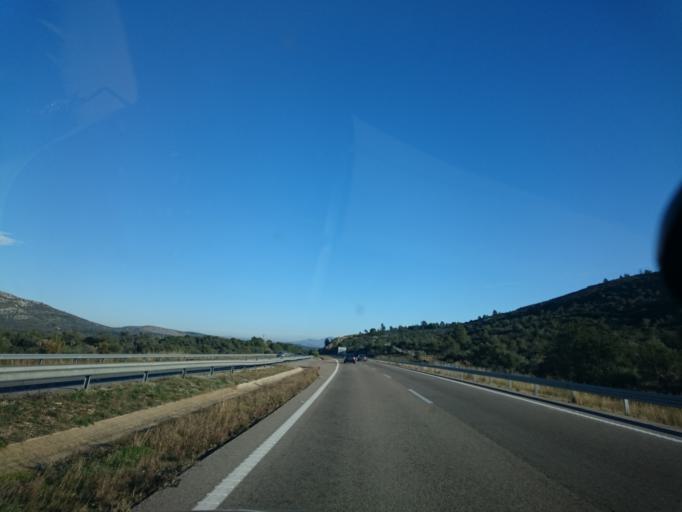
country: ES
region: Valencia
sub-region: Provincia de Castello
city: Santa Magdalena de Pulpis
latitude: 40.3791
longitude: 0.3403
